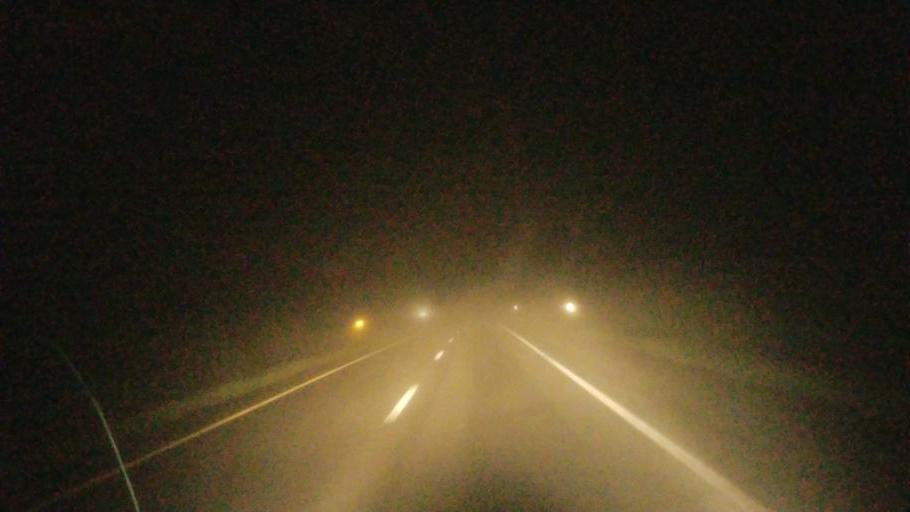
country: US
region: New York
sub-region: Cattaraugus County
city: Olean
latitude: 42.1317
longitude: -78.4143
